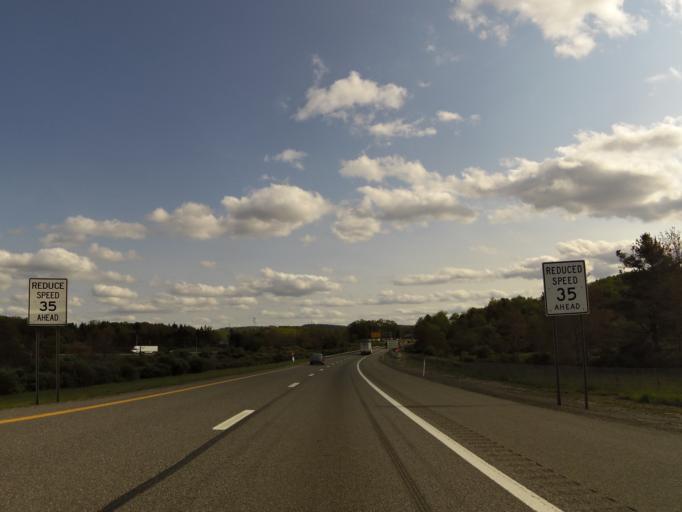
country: US
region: West Virginia
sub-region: Raleigh County
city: Shady Spring
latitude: 37.6363
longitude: -81.1117
